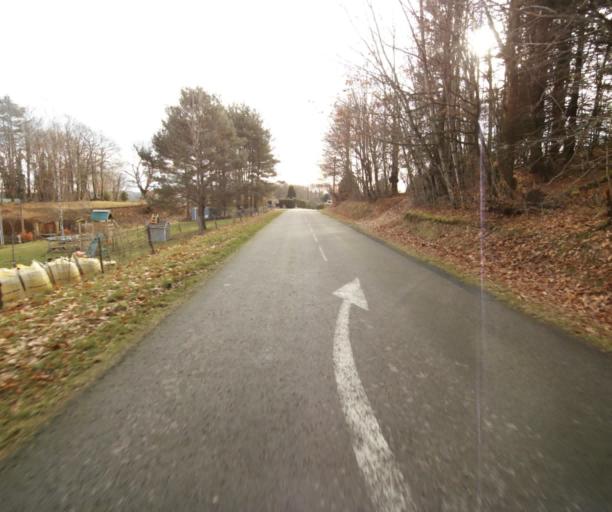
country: FR
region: Limousin
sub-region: Departement de la Correze
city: Chameyrat
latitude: 45.2434
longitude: 1.6992
